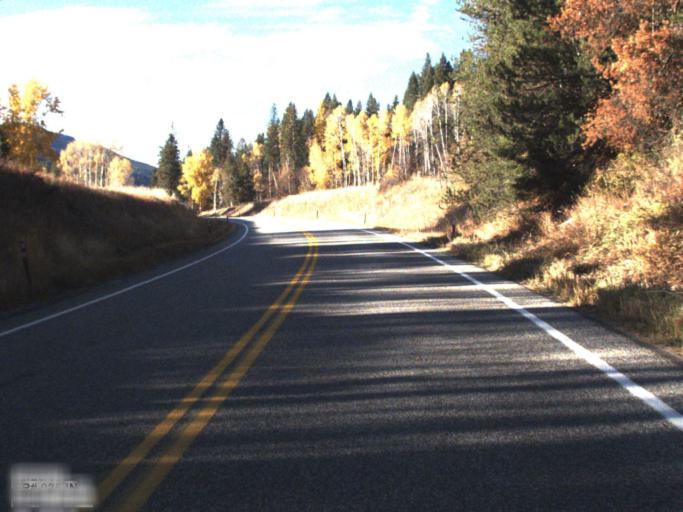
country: CA
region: British Columbia
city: Rossland
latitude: 48.9649
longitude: -117.8057
